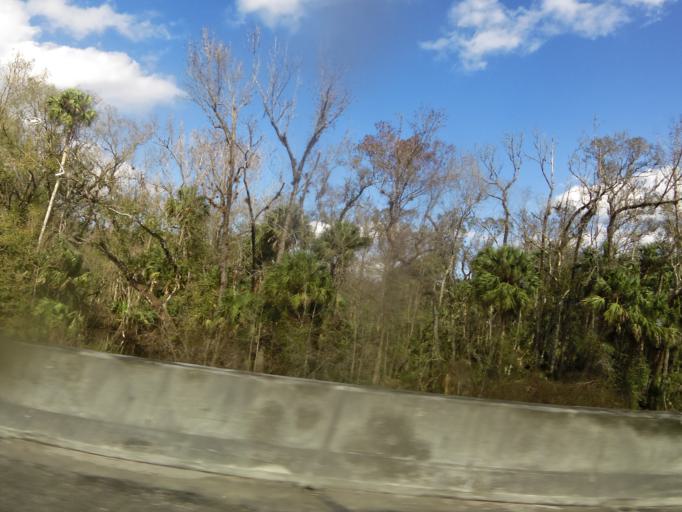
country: US
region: Florida
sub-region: Volusia County
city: De Leon Springs
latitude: 29.1634
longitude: -81.3905
